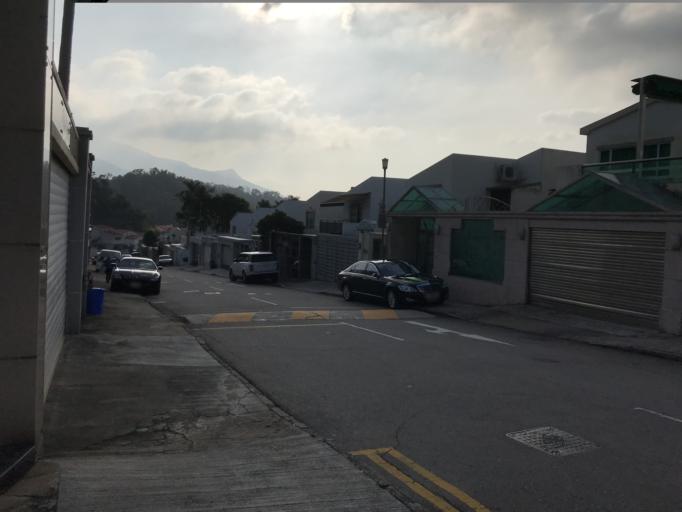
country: HK
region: Tai Po
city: Tai Po
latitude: 22.4633
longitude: 114.1596
